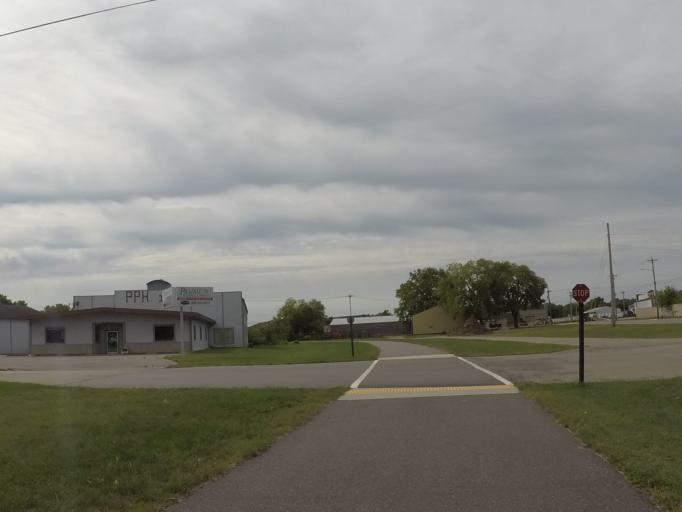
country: US
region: Wisconsin
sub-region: Sauk County
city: Sauk City
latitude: 43.2681
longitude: -89.7295
